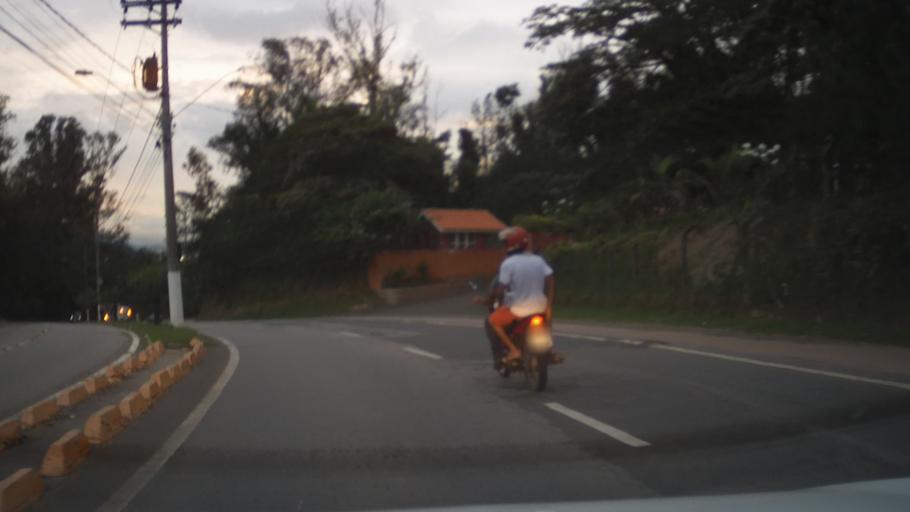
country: BR
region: Sao Paulo
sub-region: Vinhedo
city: Vinhedo
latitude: -23.0331
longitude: -46.9928
